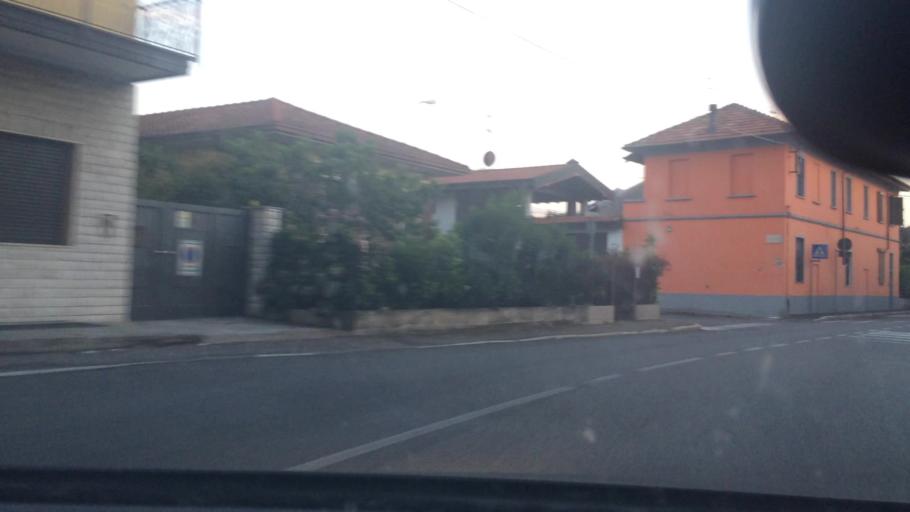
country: IT
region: Lombardy
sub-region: Citta metropolitana di Milano
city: Parabiago
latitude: 45.5422
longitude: 8.9530
